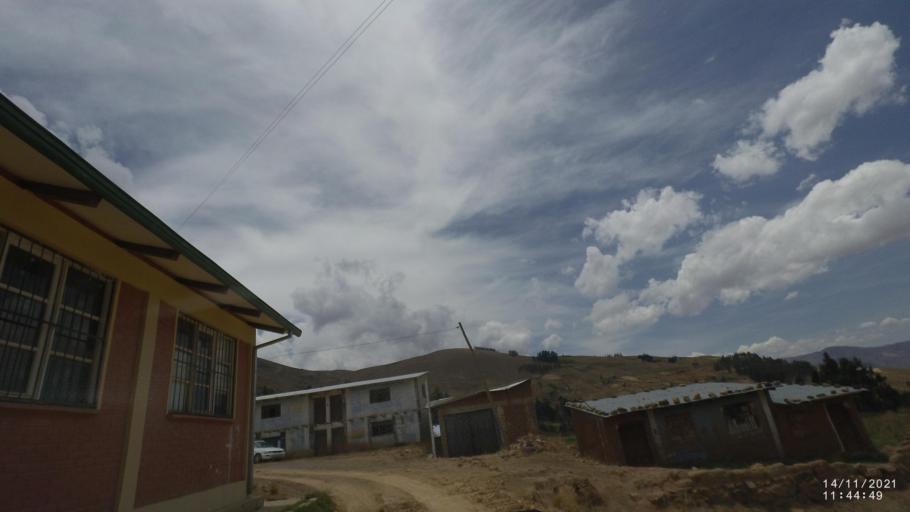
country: BO
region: Cochabamba
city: Colomi
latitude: -17.3531
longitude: -65.9901
